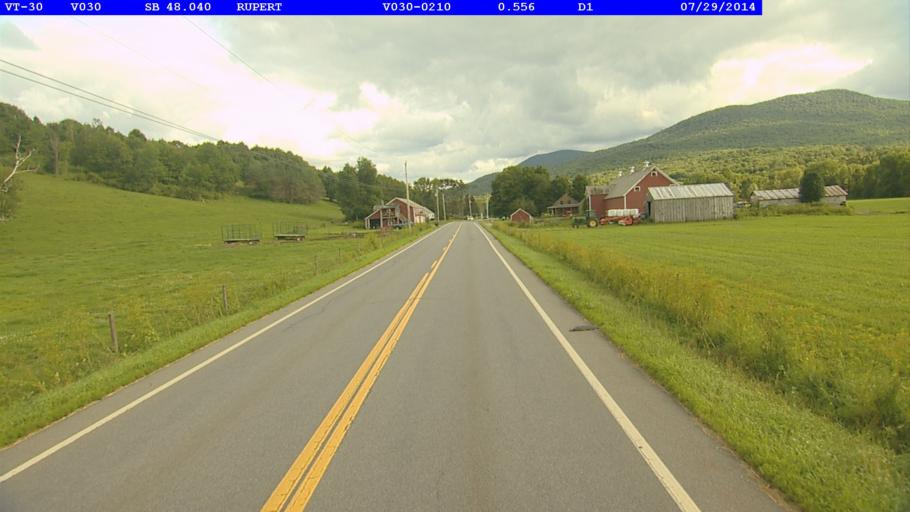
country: US
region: Vermont
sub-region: Bennington County
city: Manchester Center
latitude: 43.2788
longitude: -73.1249
